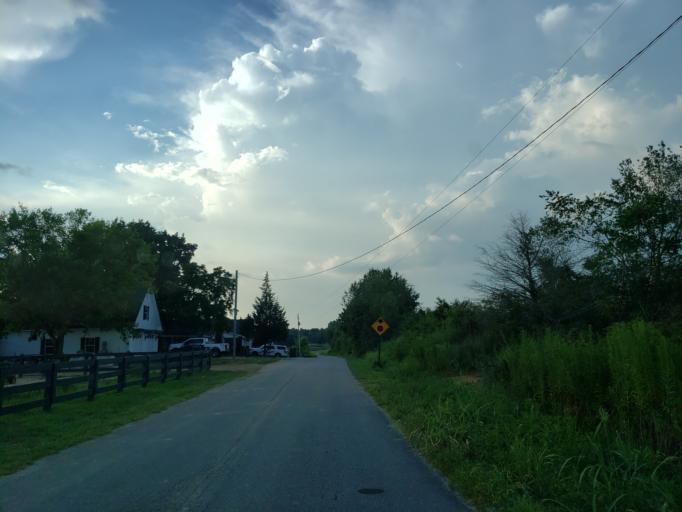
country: US
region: Georgia
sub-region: Bartow County
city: Euharlee
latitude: 34.0697
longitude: -84.9626
